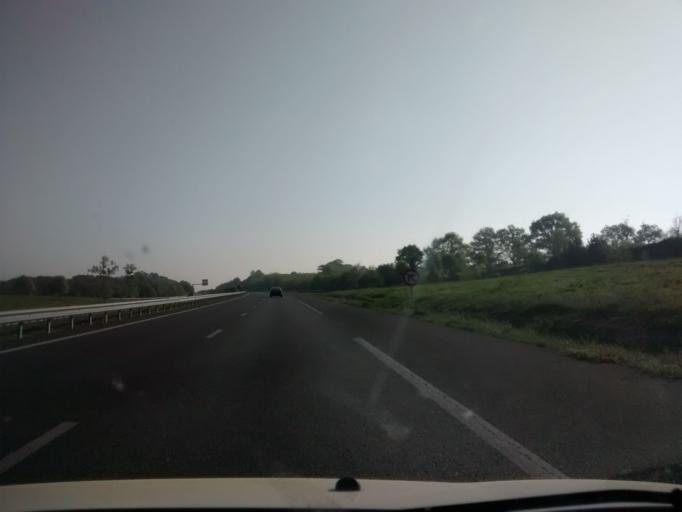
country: FR
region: Brittany
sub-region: Departement d'Ille-et-Vilaine
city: Liffre
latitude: 48.2221
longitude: -1.4981
